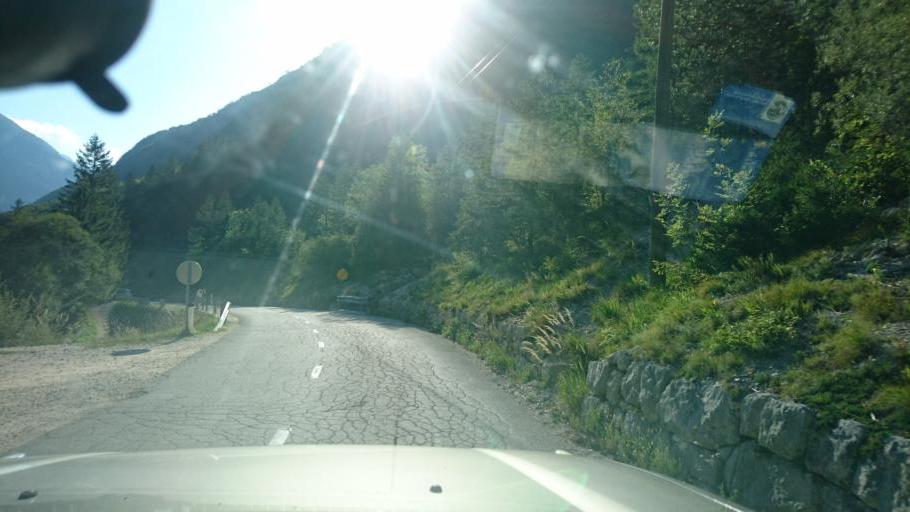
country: SI
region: Kranjska Gora
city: Kranjska Gora
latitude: 46.3574
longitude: 13.7002
